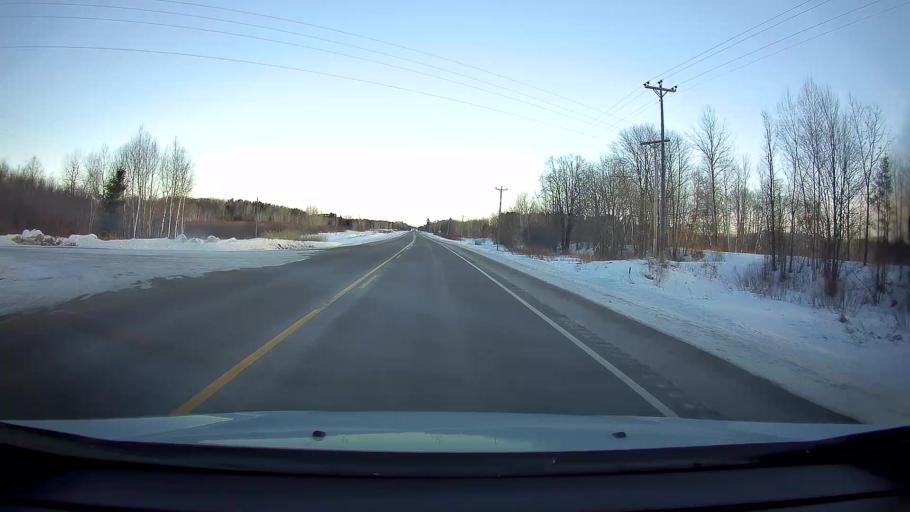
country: US
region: Wisconsin
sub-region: Washburn County
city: Shell Lake
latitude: 45.7108
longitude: -91.9439
